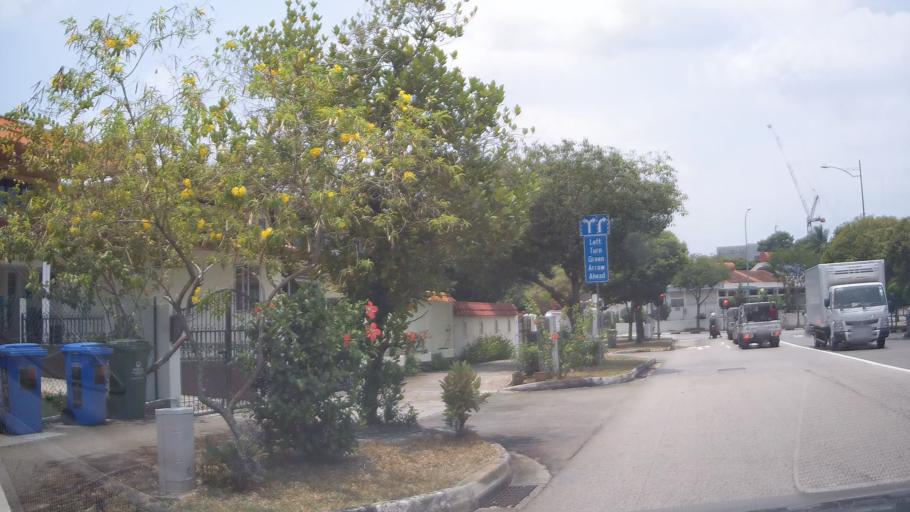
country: SG
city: Singapore
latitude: 1.3147
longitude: 103.7553
